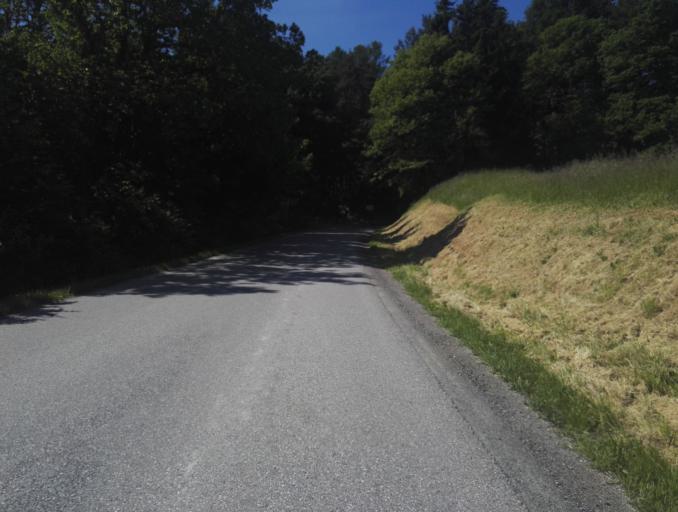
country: AT
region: Styria
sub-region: Politischer Bezirk Graz-Umgebung
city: Edelsgrub
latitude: 47.0560
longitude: 15.5807
